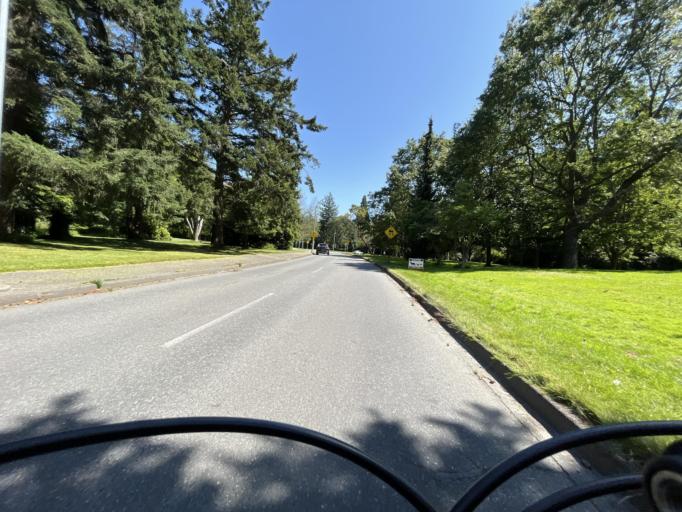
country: CA
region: British Columbia
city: Oak Bay
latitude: 48.4613
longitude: -123.3154
